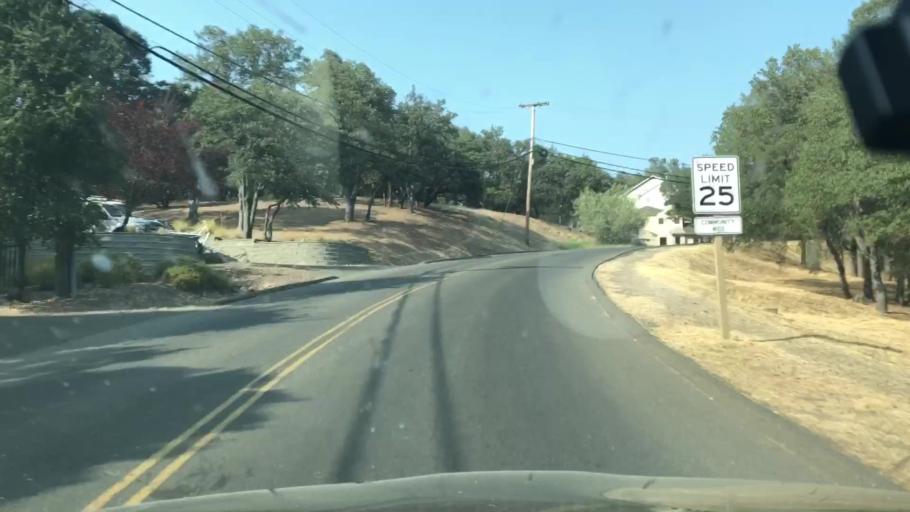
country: US
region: California
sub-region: Lake County
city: Hidden Valley Lake
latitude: 38.8033
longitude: -122.5608
